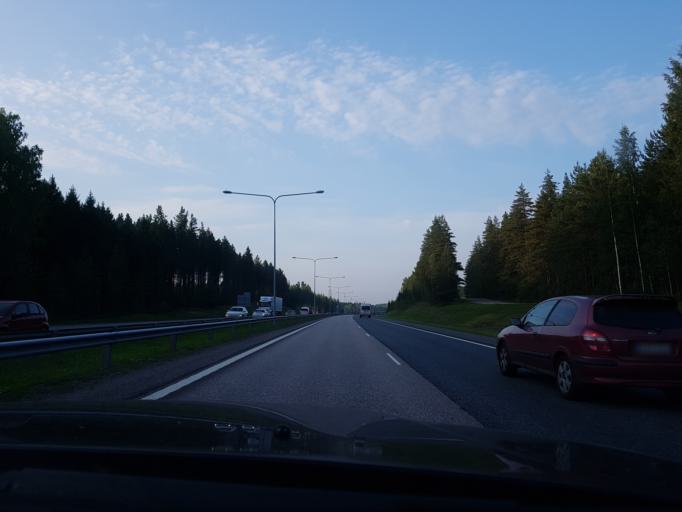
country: FI
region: Uusimaa
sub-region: Helsinki
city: Tuusula
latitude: 60.3517
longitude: 25.0003
